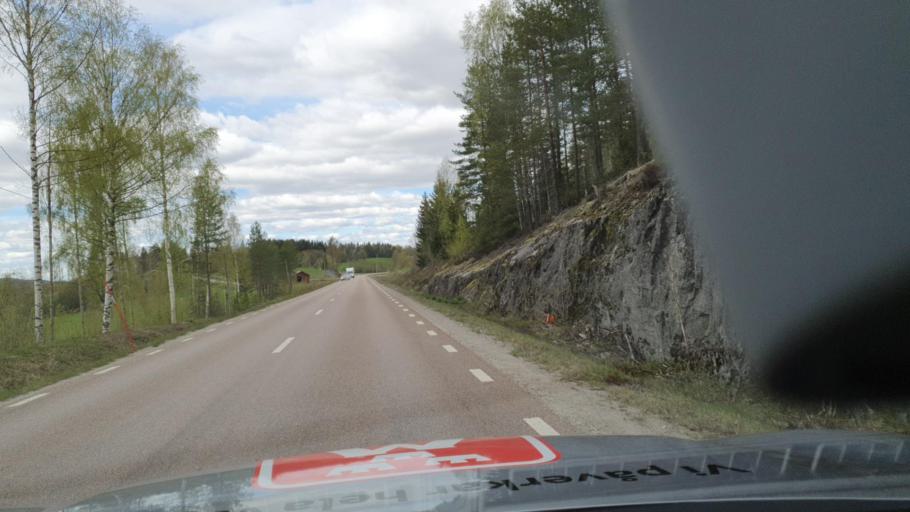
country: SE
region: Vaesternorrland
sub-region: OErnskoeldsviks Kommun
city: Ornskoldsvik
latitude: 63.5203
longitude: 18.7305
